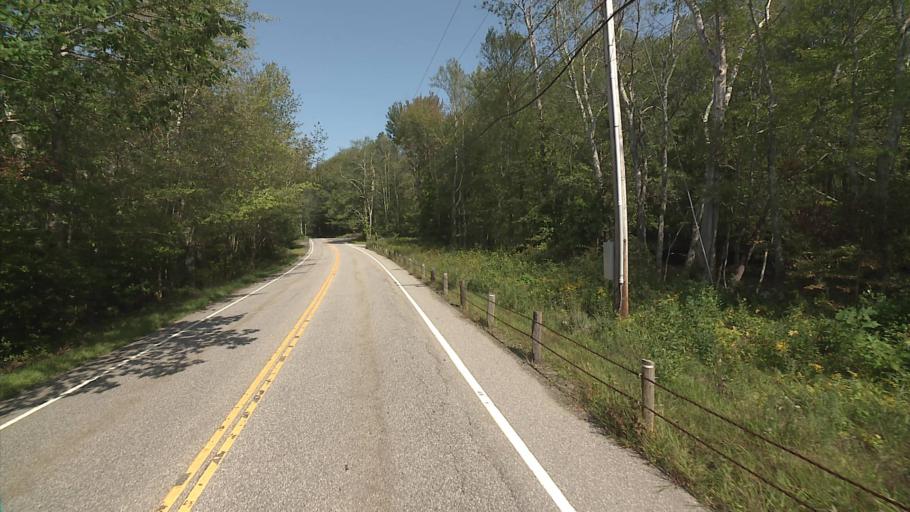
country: US
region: Connecticut
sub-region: Windham County
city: East Brooklyn
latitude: 41.8066
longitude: -71.9519
